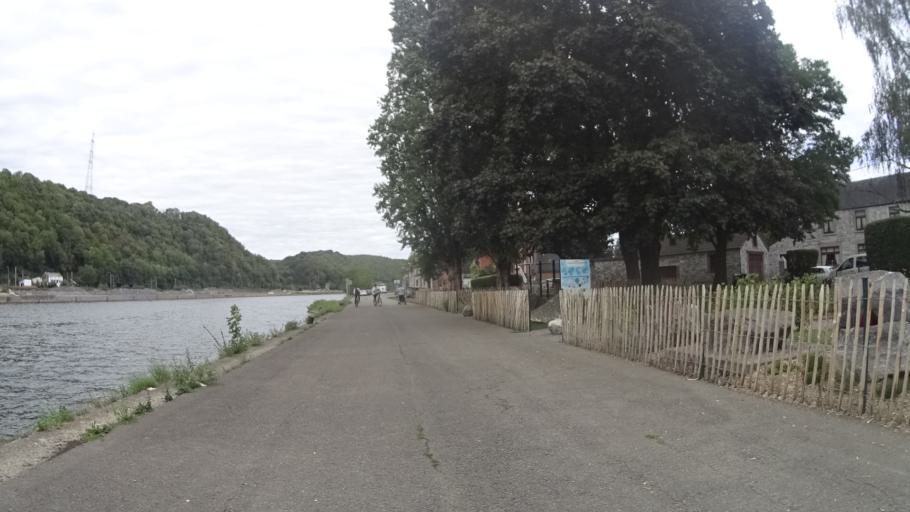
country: BE
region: Wallonia
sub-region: Province de Namur
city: Andenne
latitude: 50.4908
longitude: 5.0273
